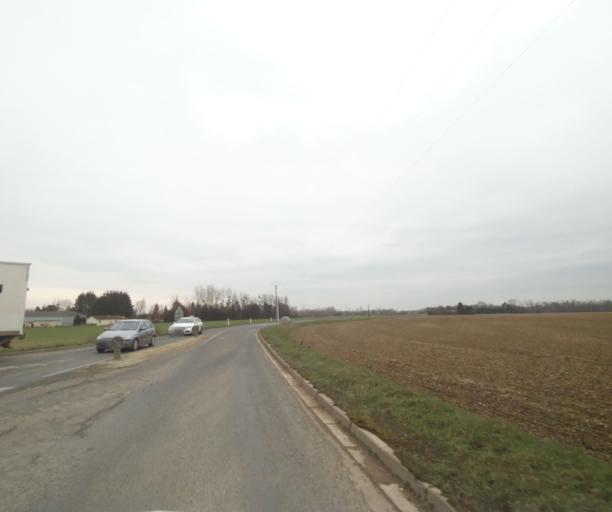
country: FR
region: Champagne-Ardenne
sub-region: Departement de la Haute-Marne
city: Villiers-en-Lieu
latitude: 48.6567
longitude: 4.9094
